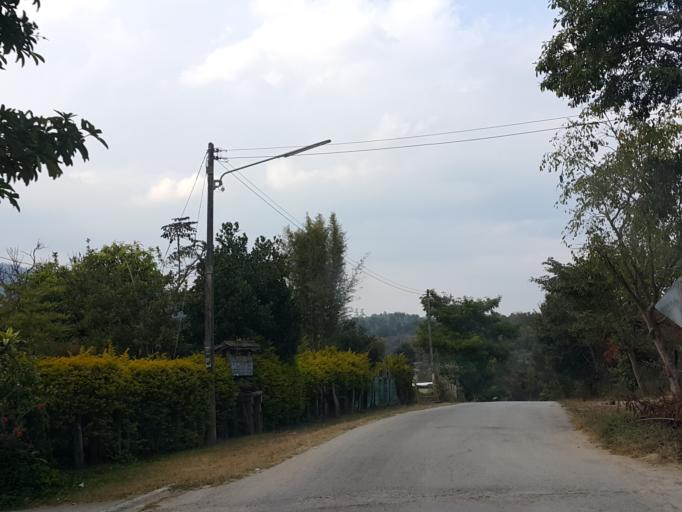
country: TH
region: Chiang Mai
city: Om Koi
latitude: 17.8021
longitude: 98.3335
